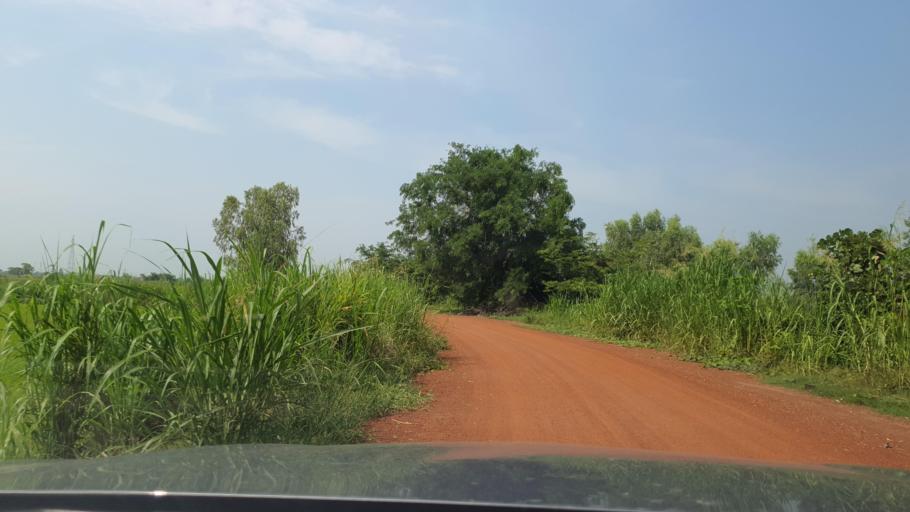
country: TH
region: Phitsanulok
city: Bang Rakam
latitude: 16.7888
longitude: 100.1092
